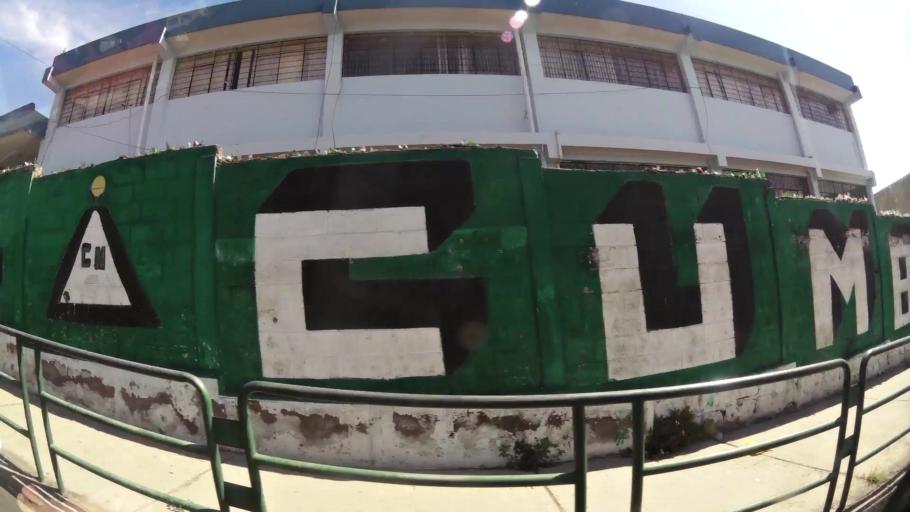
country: EC
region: Pichincha
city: Quito
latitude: -0.2030
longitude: -78.4399
